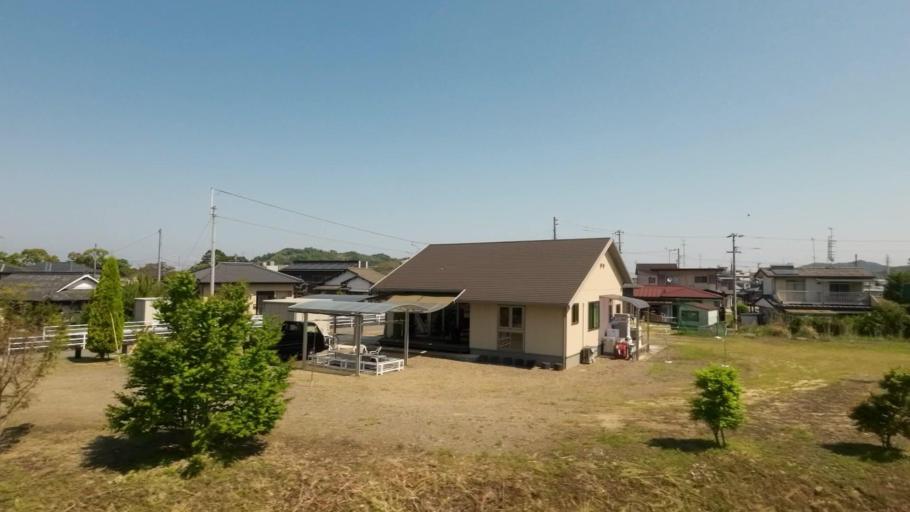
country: JP
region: Ehime
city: Niihama
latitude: 33.9706
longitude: 133.3286
